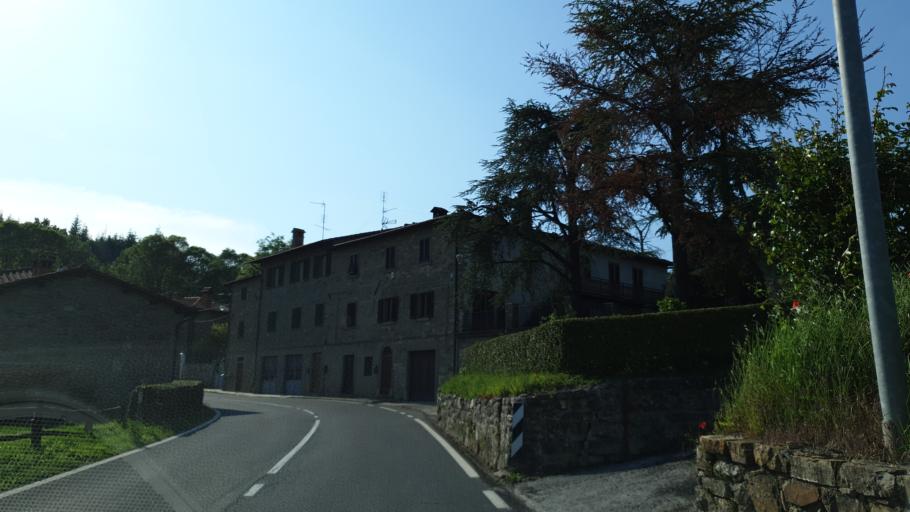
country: IT
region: Tuscany
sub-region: Province of Arezzo
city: Stia
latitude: 43.7762
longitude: 11.6929
